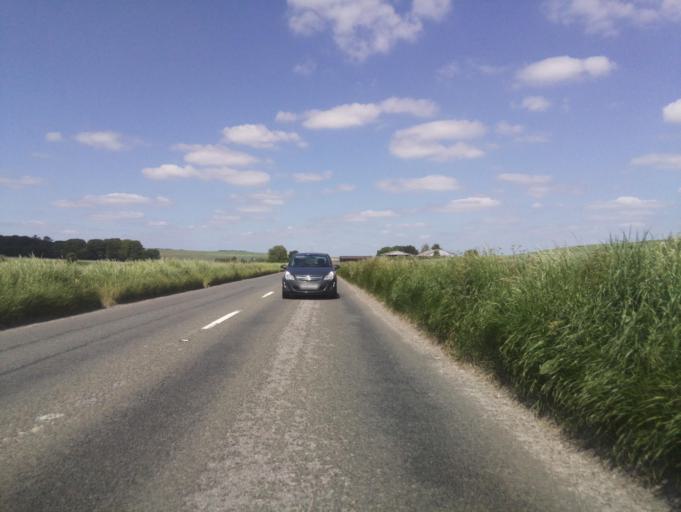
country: GB
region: England
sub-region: Wiltshire
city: Devizes
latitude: 51.3931
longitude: -1.9397
